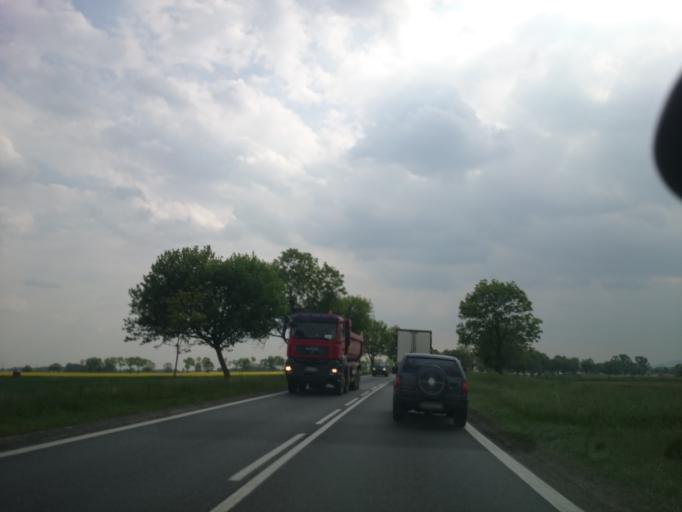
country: PL
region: Lower Silesian Voivodeship
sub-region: Powiat wroclawski
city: Kobierzyce
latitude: 50.9751
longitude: 16.9443
